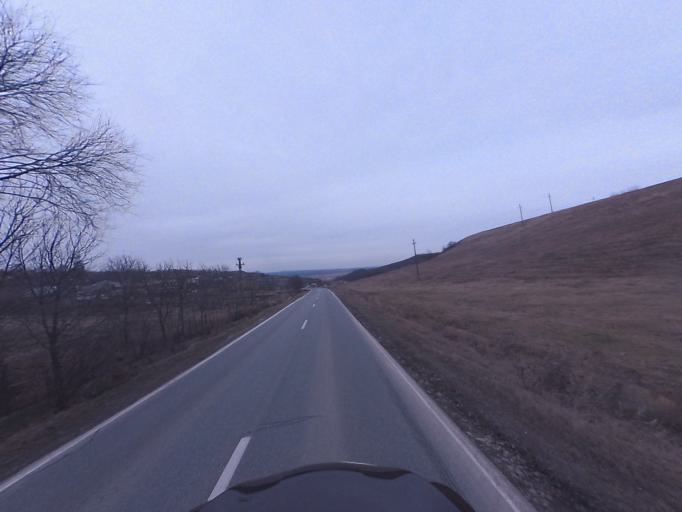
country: RO
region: Iasi
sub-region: Comuna Popricani
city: Popricani
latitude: 47.2922
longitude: 27.5111
